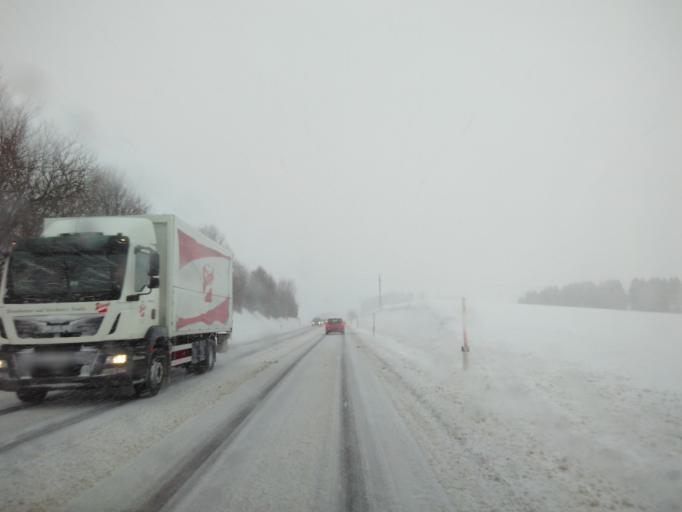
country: AT
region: Upper Austria
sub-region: Politischer Bezirk Urfahr-Umgebung
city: Bad Leonfelden
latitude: 48.5055
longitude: 14.2951
